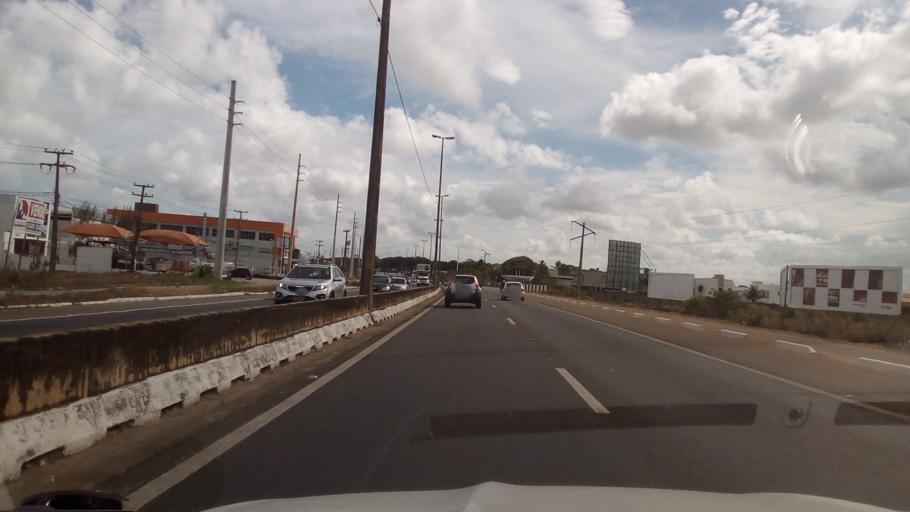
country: BR
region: Paraiba
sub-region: Joao Pessoa
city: Joao Pessoa
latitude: -7.0523
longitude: -34.8501
